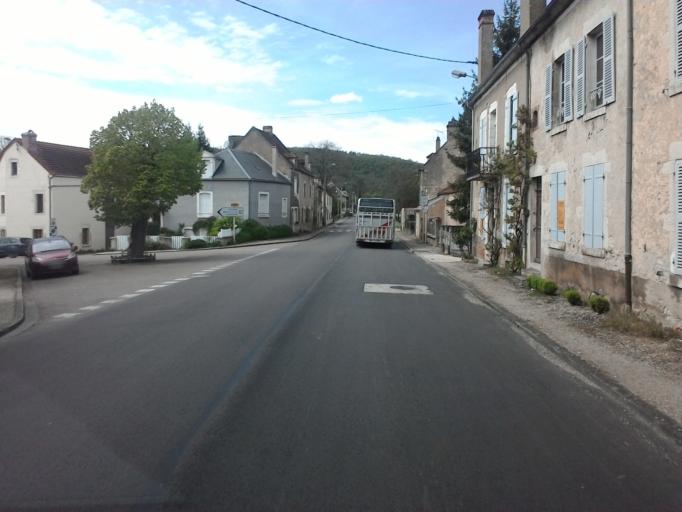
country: FR
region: Bourgogne
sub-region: Departement de l'Yonne
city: Joux-la-Ville
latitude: 47.5619
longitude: 3.7844
